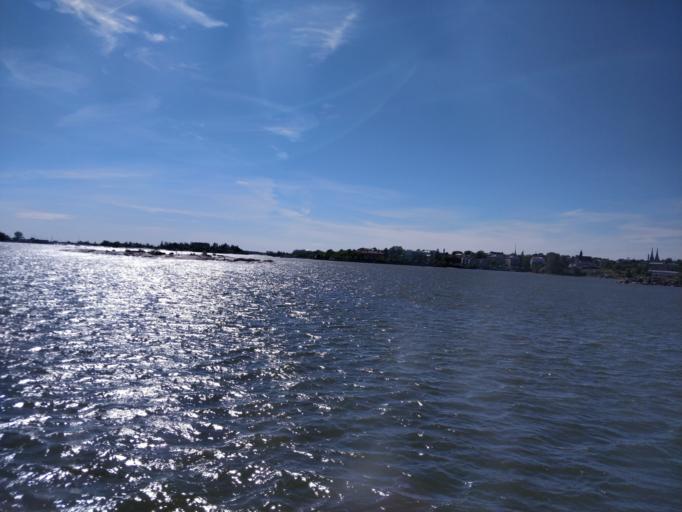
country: FI
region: Uusimaa
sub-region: Helsinki
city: Helsinki
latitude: 60.1588
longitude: 24.9798
